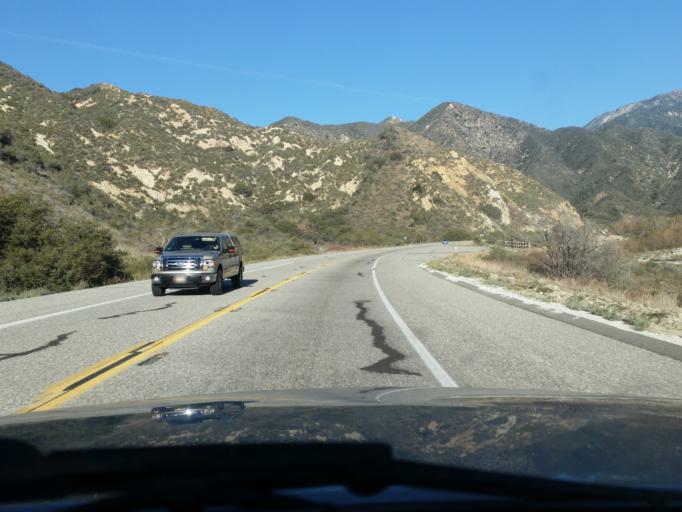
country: US
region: California
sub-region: San Bernardino County
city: Yucaipa
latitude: 34.1000
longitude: -117.0260
